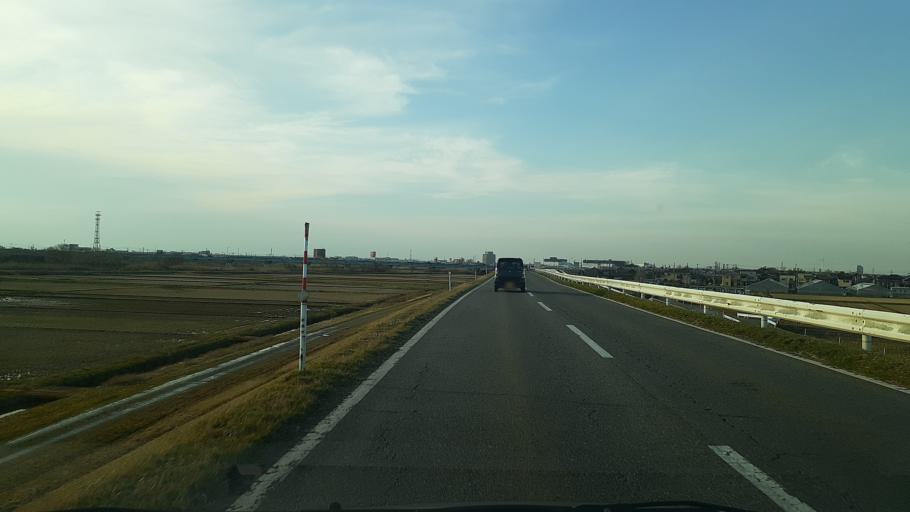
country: JP
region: Niigata
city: Niigata-shi
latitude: 37.8502
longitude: 139.0271
